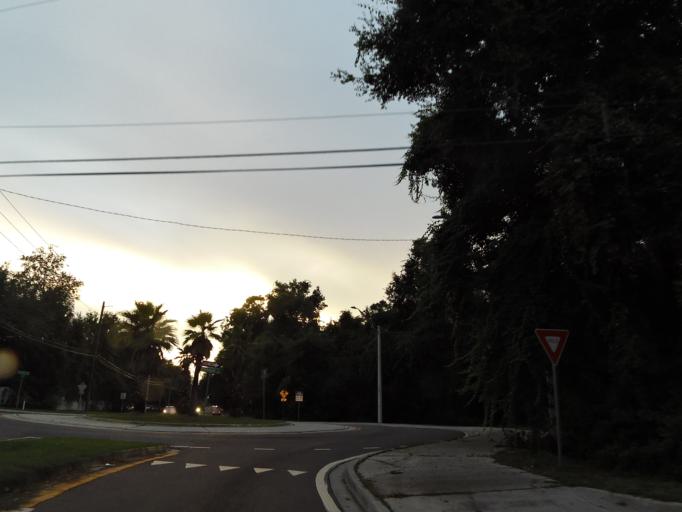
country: US
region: Florida
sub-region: Duval County
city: Jacksonville
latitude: 30.3669
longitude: -81.5608
